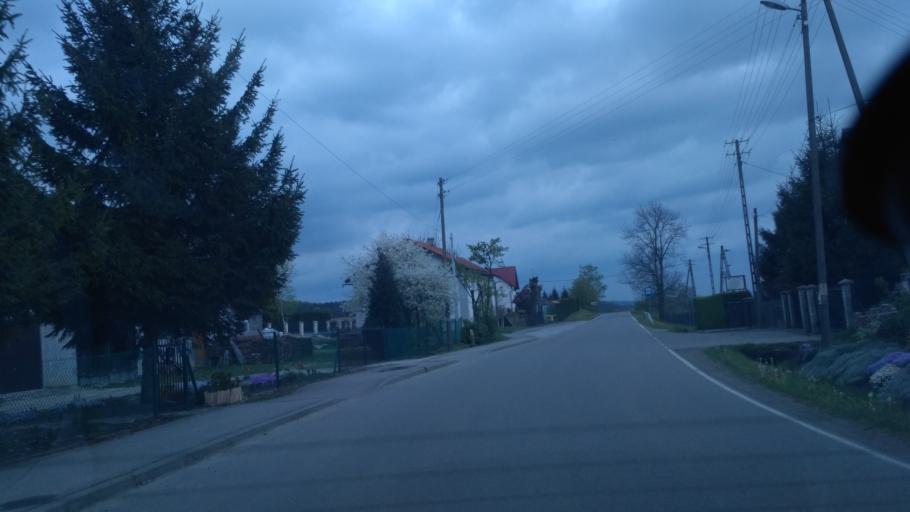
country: PL
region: Subcarpathian Voivodeship
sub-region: Powiat brzozowski
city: Turze Pole
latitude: 49.6397
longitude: 22.0000
